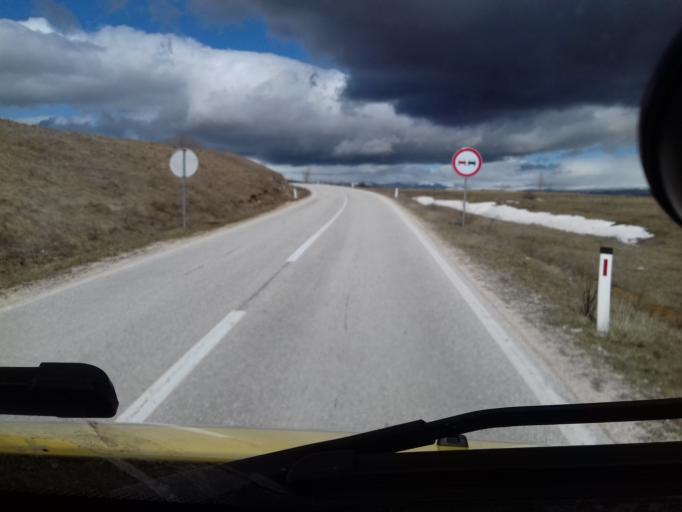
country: BA
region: Federation of Bosnia and Herzegovina
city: Dreznica
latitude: 43.6173
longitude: 17.2644
